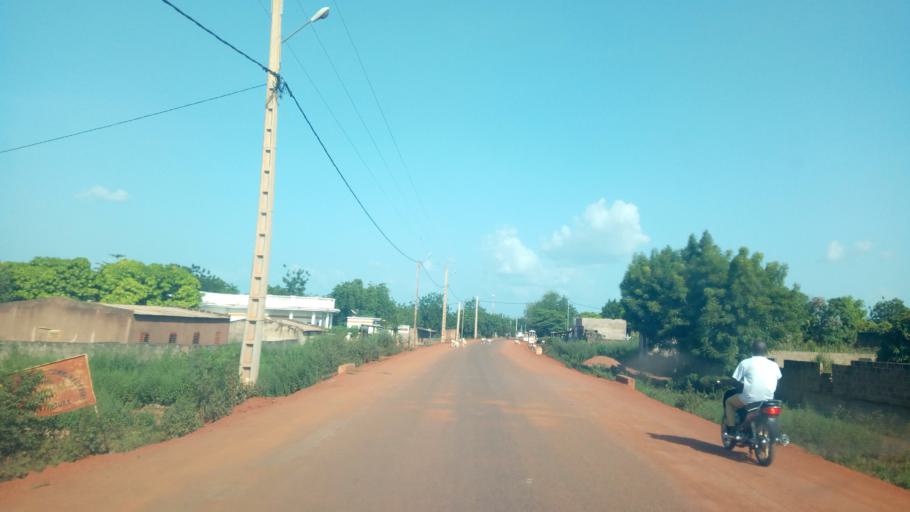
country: ML
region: Sikasso
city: Yorosso
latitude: 12.1848
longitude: -4.8121
